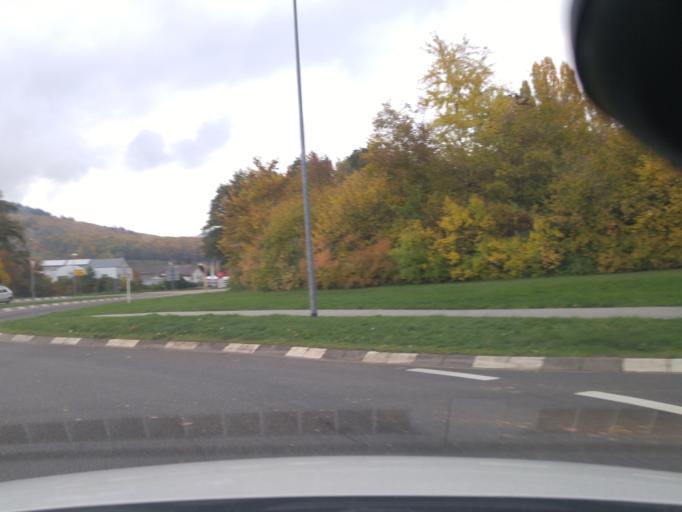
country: DE
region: Rheinland-Pfalz
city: Annweiler am Trifels
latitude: 49.2114
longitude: 7.9819
